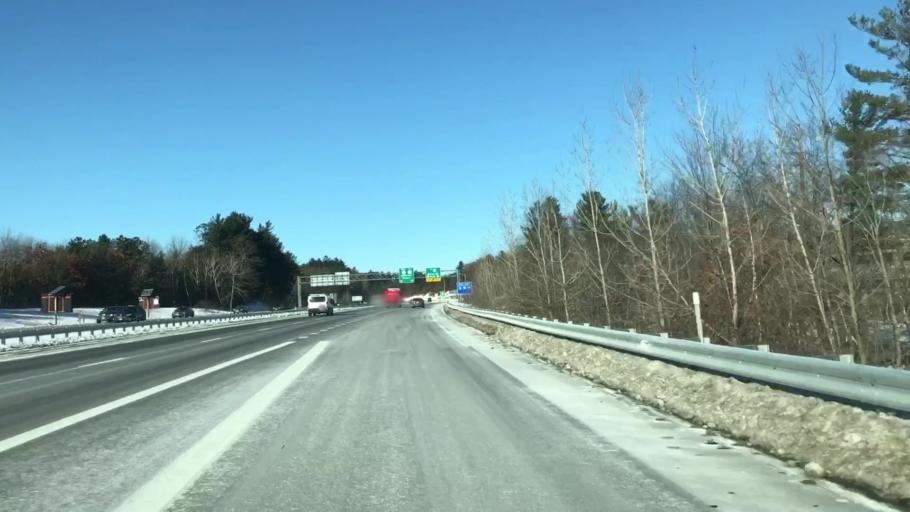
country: US
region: New Hampshire
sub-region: Hillsborough County
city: Bedford
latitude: 42.9534
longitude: -71.4821
